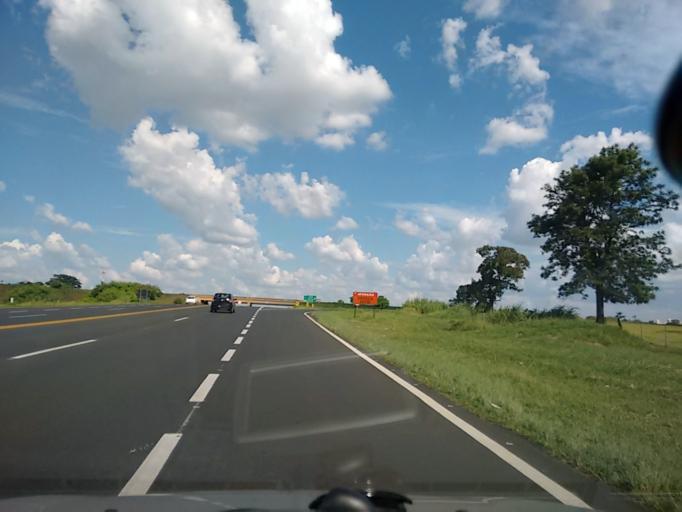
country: BR
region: Sao Paulo
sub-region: Marilia
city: Marilia
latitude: -22.1776
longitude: -49.9739
